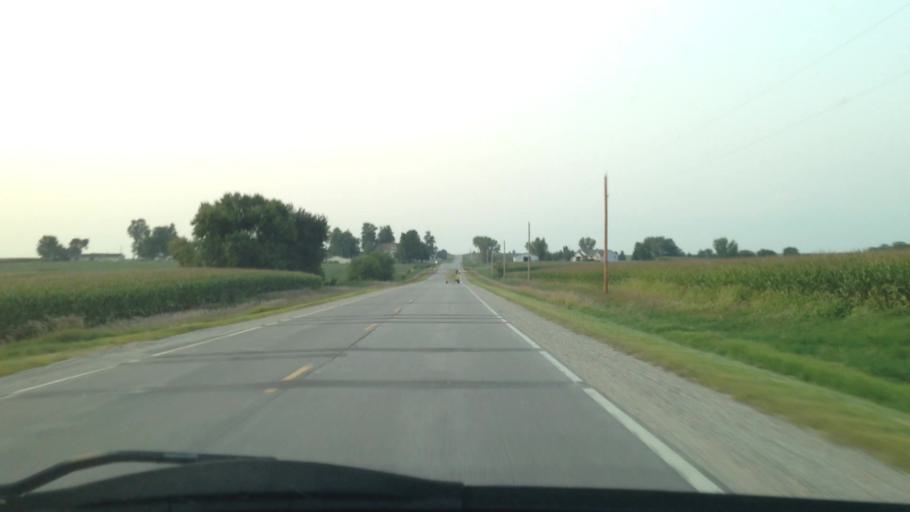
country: US
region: Iowa
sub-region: Benton County
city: Atkins
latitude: 42.0021
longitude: -91.8735
